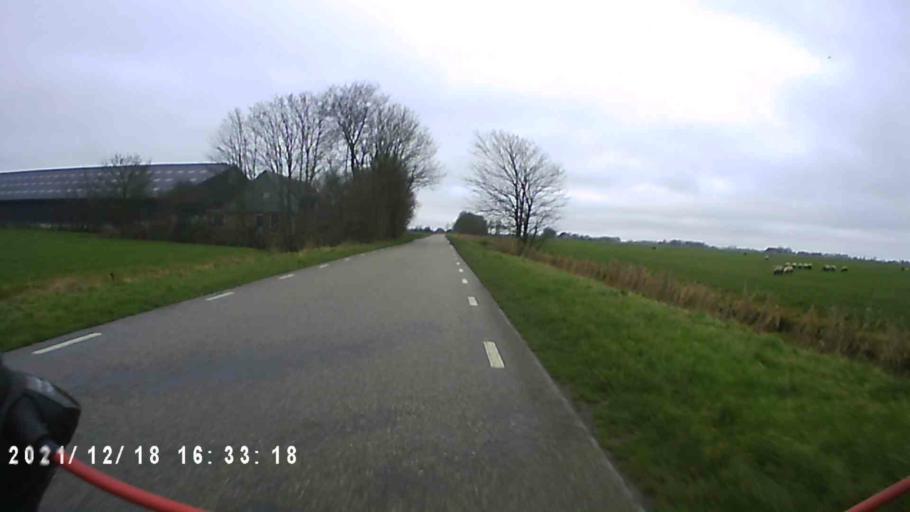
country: NL
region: Friesland
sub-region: Gemeente Dongeradeel
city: Dokkum
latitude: 53.3566
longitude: 6.0303
